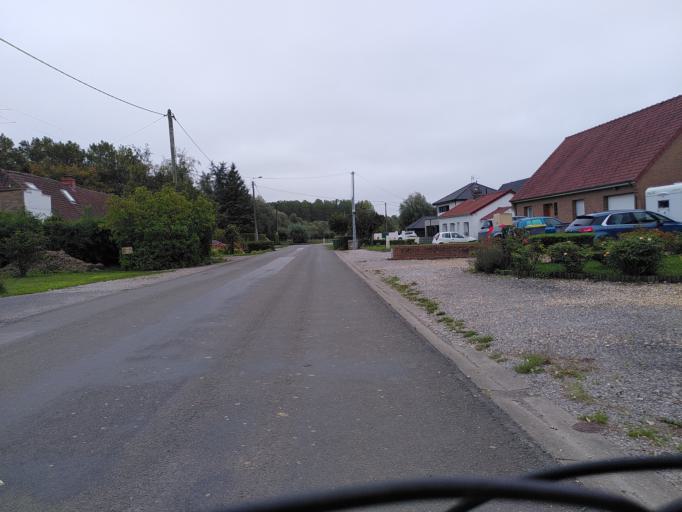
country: FR
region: Nord-Pas-de-Calais
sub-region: Departement du Pas-de-Calais
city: Saint-Venant
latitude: 50.6269
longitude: 2.5383
